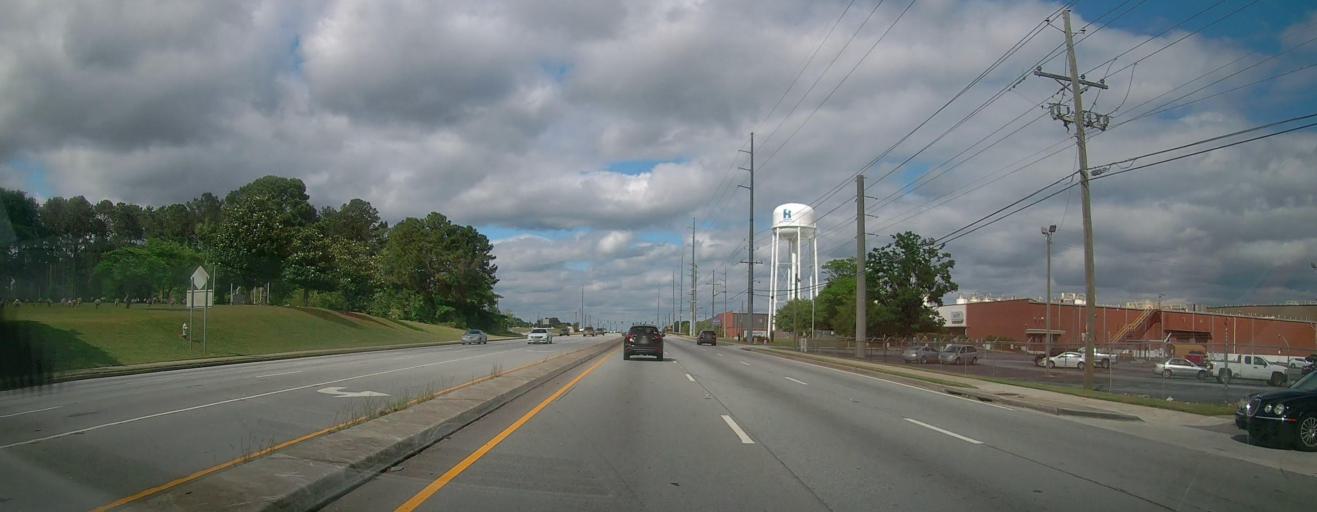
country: US
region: Georgia
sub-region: Rockdale County
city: Conyers
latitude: 33.6594
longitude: -83.9992
